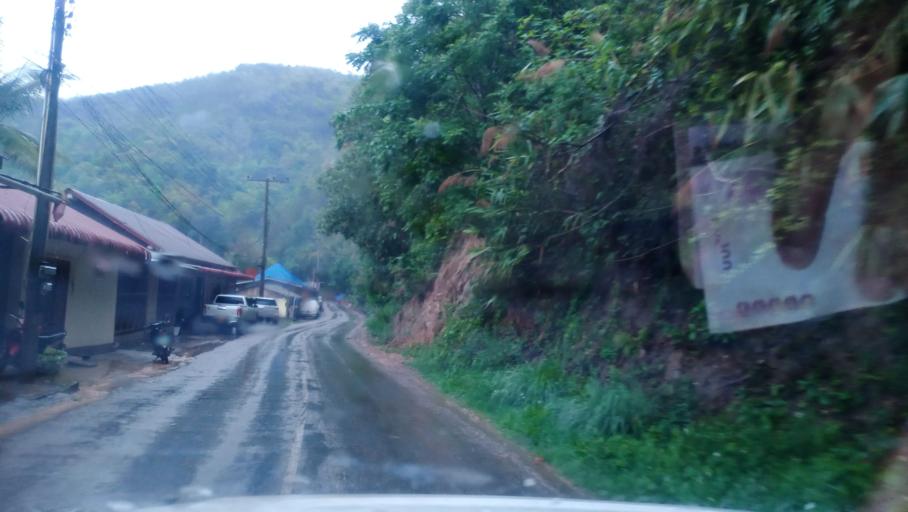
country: LA
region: Phongsali
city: Khoa
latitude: 21.0806
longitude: 102.5038
